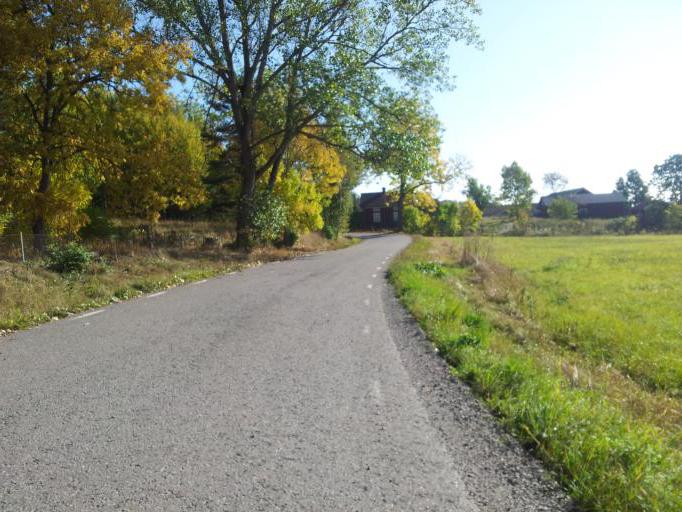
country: SE
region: Stockholm
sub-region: Norrtalje Kommun
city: Nykvarn
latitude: 59.8486
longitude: 18.1283
